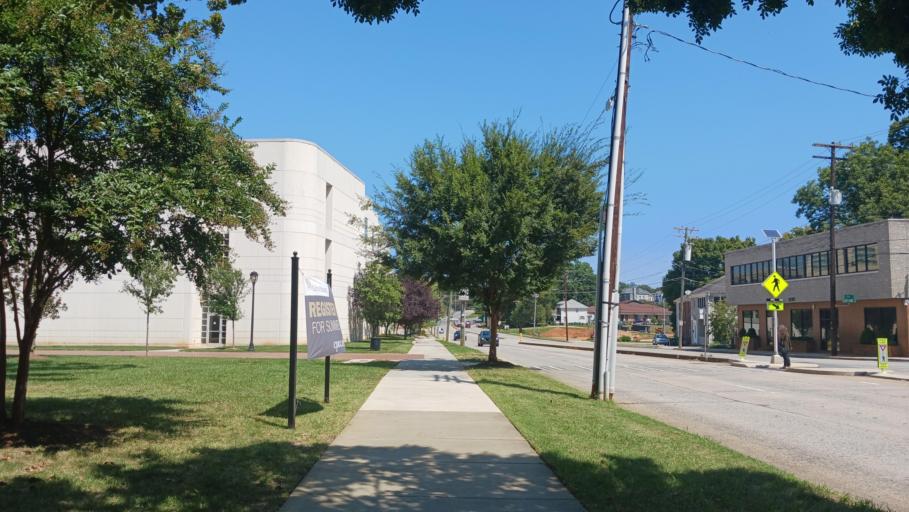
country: US
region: North Carolina
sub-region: Mecklenburg County
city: Charlotte
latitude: 35.2163
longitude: -80.8284
